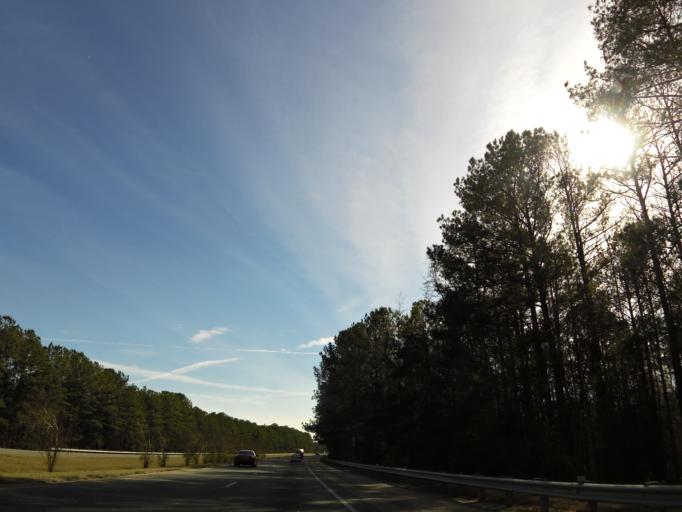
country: US
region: Georgia
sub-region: Harris County
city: Hamilton
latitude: 32.7558
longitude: -85.0165
